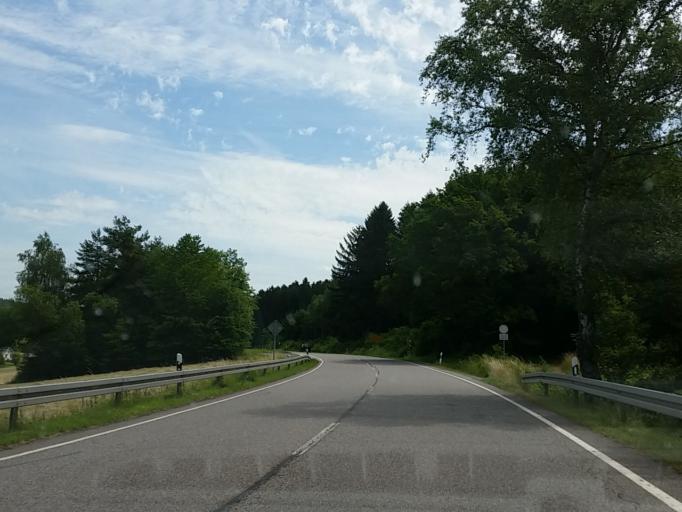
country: DE
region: Saarland
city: Britten
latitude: 49.5252
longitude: 6.6955
